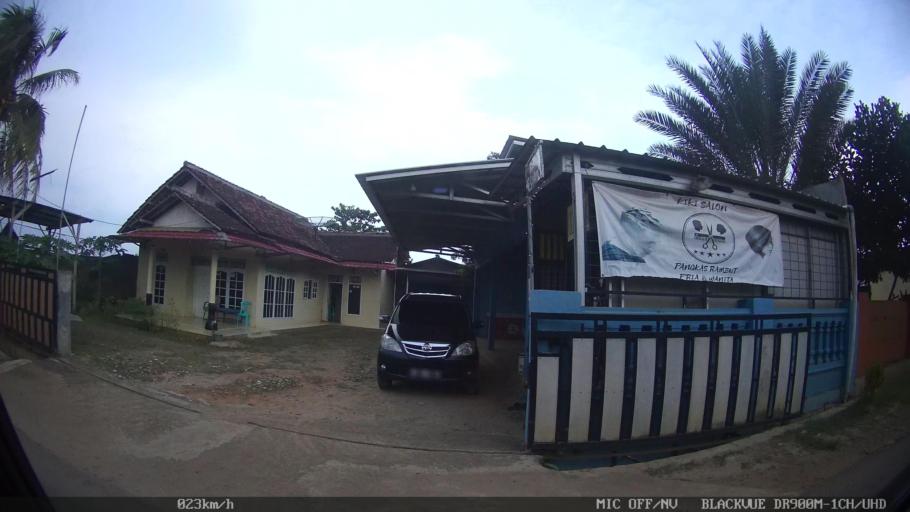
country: ID
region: Lampung
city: Kedaton
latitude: -5.3482
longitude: 105.2311
